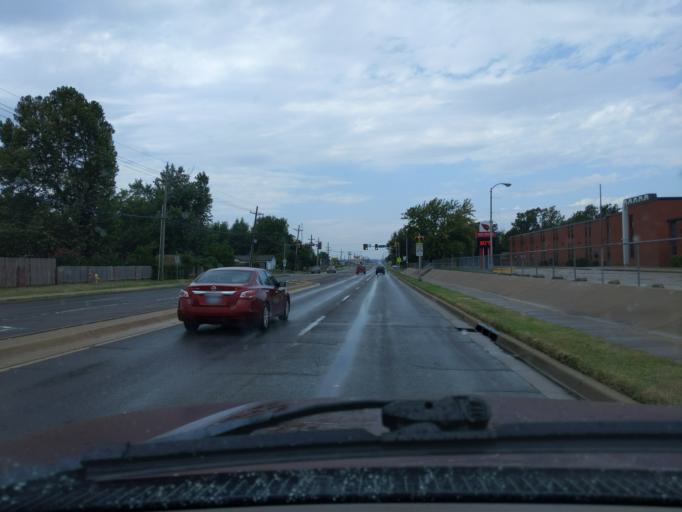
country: US
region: Oklahoma
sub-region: Tulsa County
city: Broken Arrow
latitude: 36.1335
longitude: -95.8403
